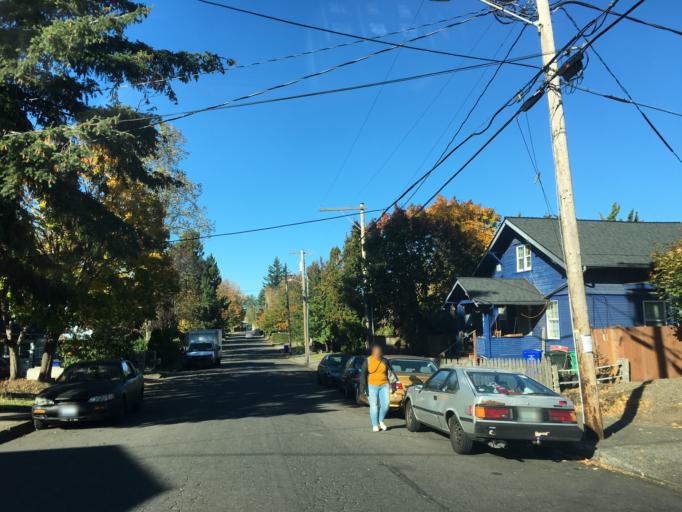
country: US
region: Oregon
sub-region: Multnomah County
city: Gresham
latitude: 45.4984
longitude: -122.4186
